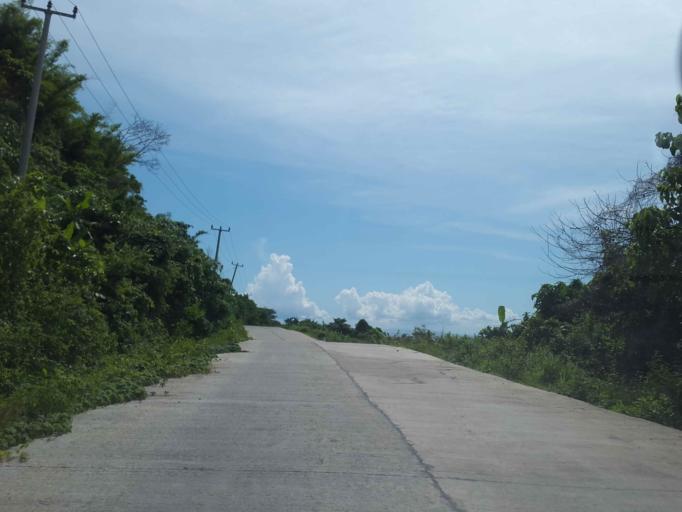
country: ID
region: Banten
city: Citeureup
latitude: -6.5085
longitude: 105.6377
